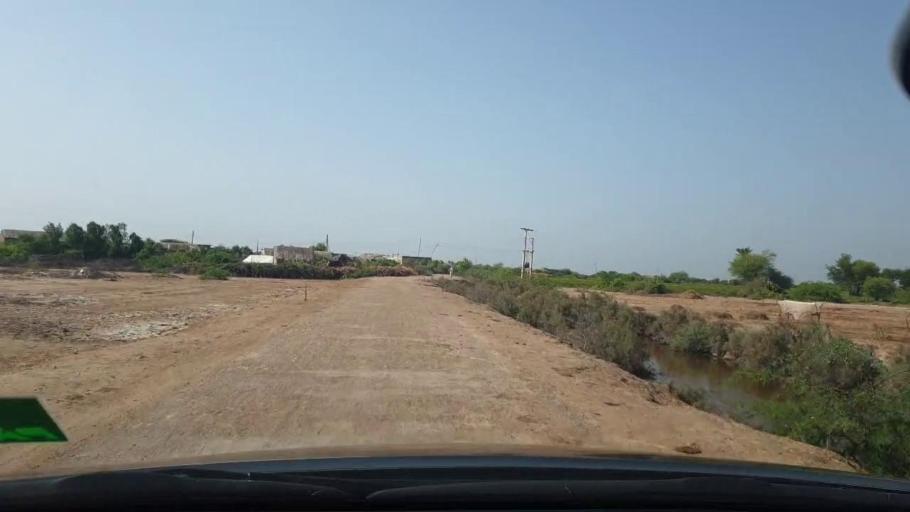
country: PK
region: Sindh
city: Tando Bago
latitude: 24.7461
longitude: 68.9861
